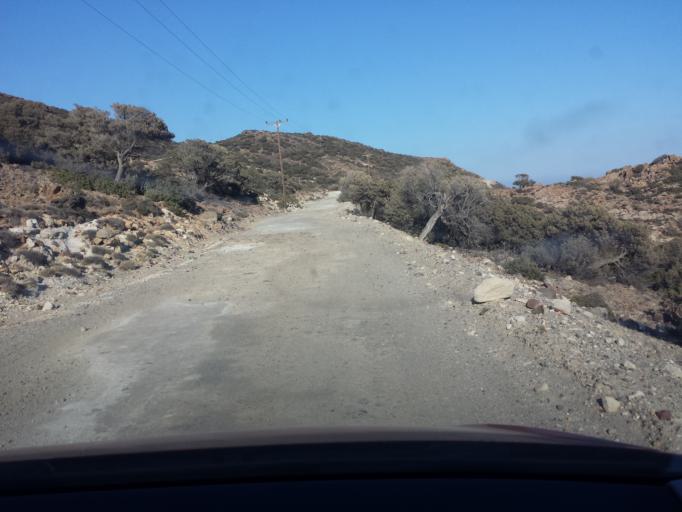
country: GR
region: South Aegean
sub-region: Nomos Kykladon
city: Adamas
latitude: 36.6575
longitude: 24.3757
